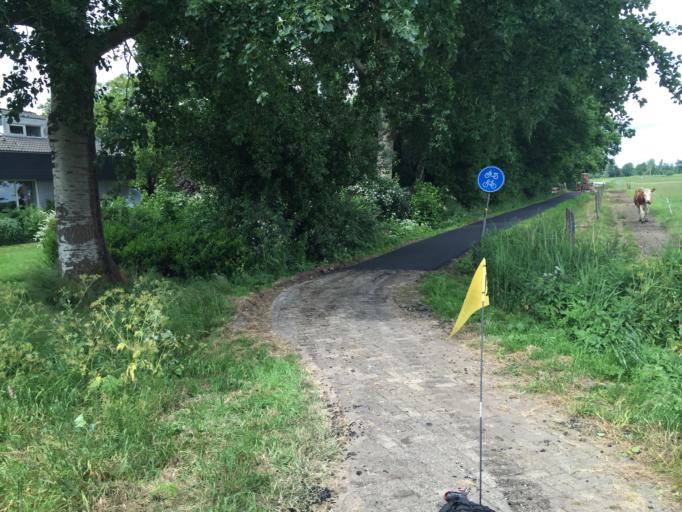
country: NL
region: Drenthe
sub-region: Gemeente Westerveld
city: Dwingeloo
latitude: 52.8497
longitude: 6.4669
